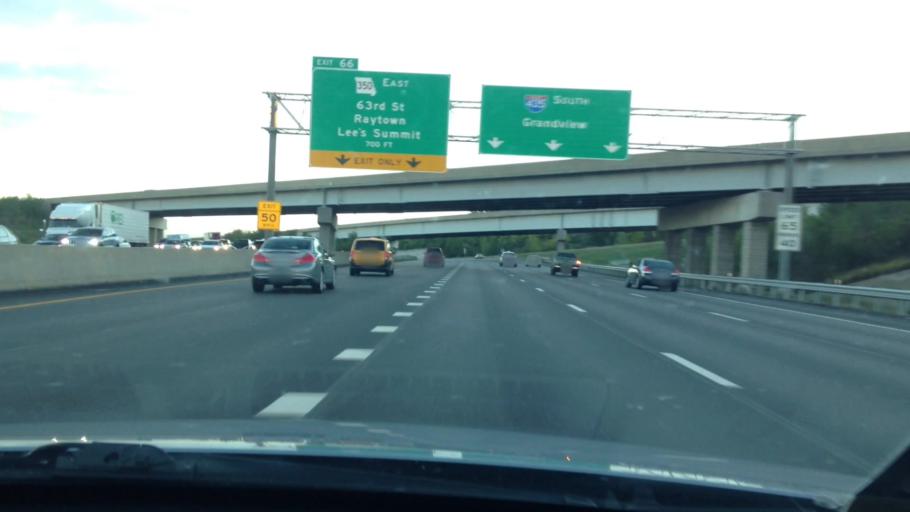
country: US
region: Missouri
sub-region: Jackson County
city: Raytown
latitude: 39.0223
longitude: -94.5010
